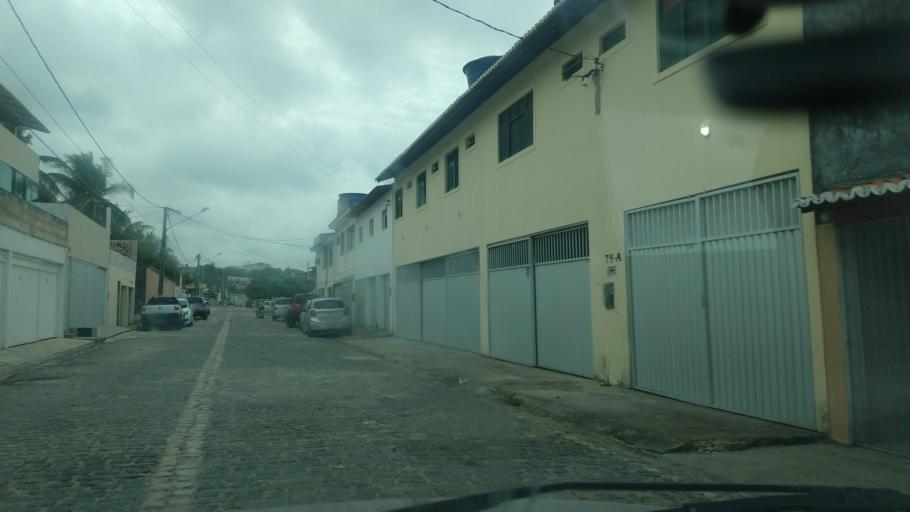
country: BR
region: Rio Grande do Norte
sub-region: Nisia Floresta
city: Nisia Floresta
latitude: -5.9745
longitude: -35.1254
